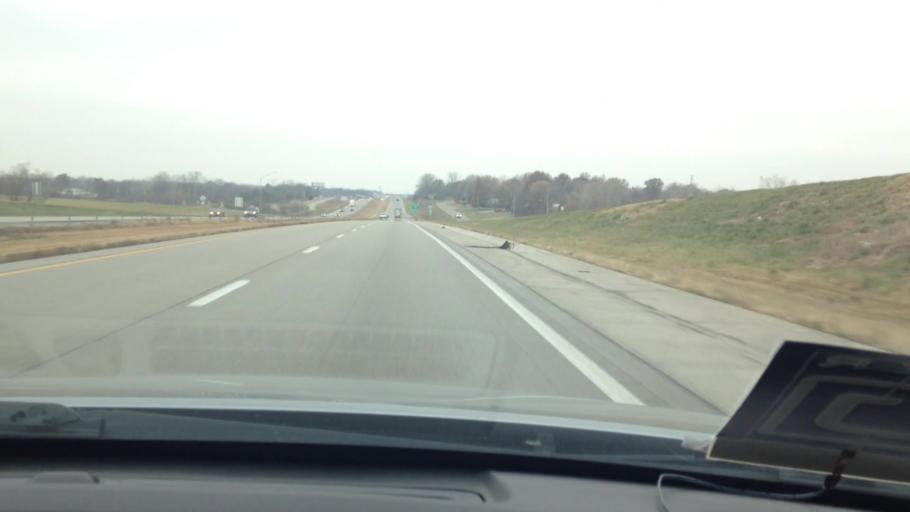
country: US
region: Missouri
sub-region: Cass County
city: Peculiar
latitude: 38.7235
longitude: -94.4552
